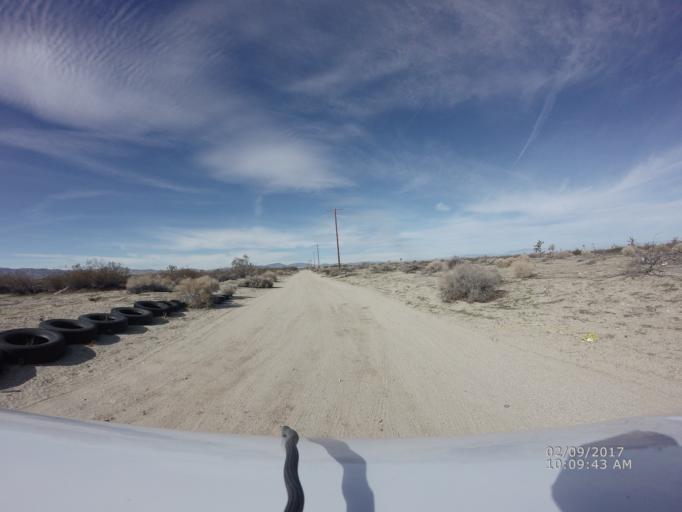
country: US
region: California
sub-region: Los Angeles County
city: Lake Los Angeles
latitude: 34.5727
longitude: -117.8874
